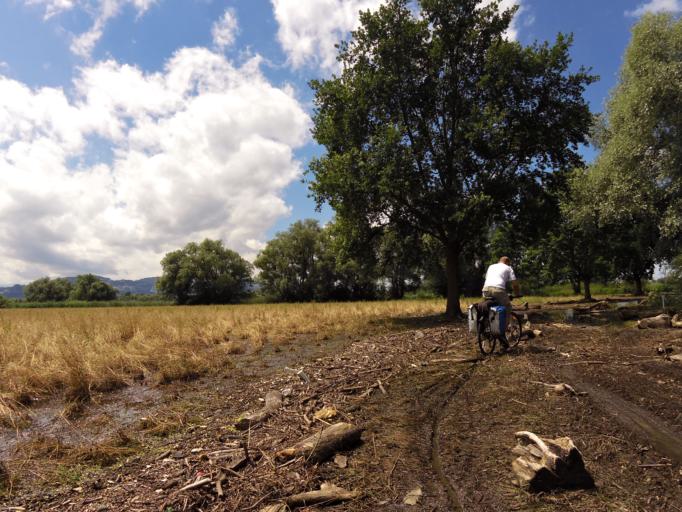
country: AT
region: Vorarlberg
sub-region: Politischer Bezirk Bregenz
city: Hard
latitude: 47.4975
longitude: 9.6773
